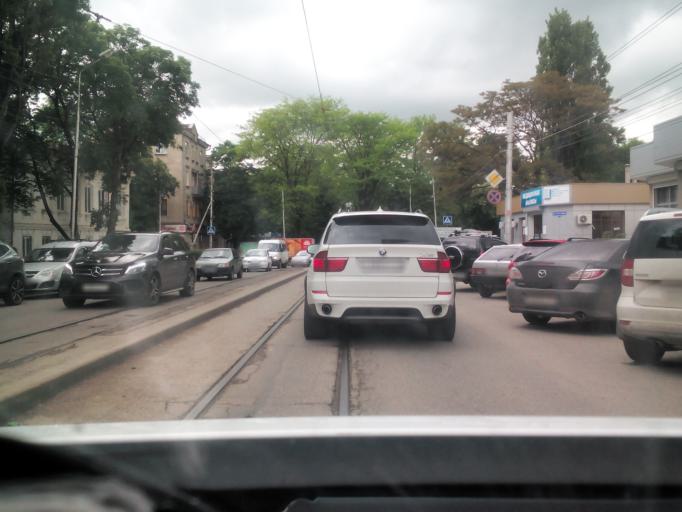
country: RU
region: Stavropol'skiy
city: Pyatigorsk
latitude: 44.0375
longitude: 43.0645
